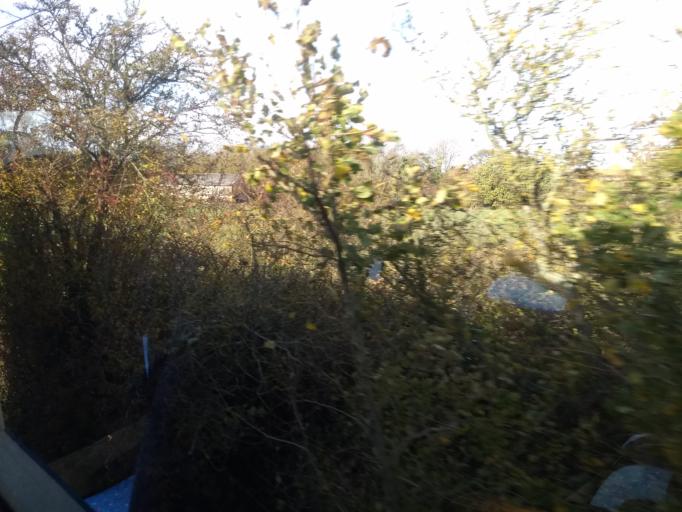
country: GB
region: England
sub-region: Isle of Wight
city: Shalfleet
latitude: 50.6914
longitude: -1.4443
